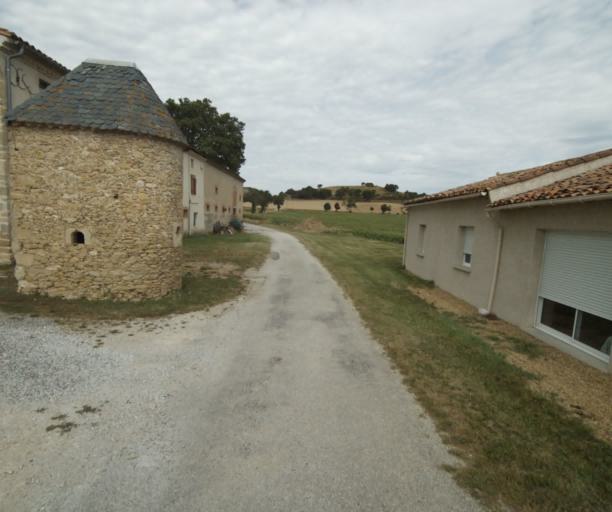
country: FR
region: Midi-Pyrenees
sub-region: Departement de la Haute-Garonne
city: Saint-Felix-Lauragais
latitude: 43.4351
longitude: 1.9012
